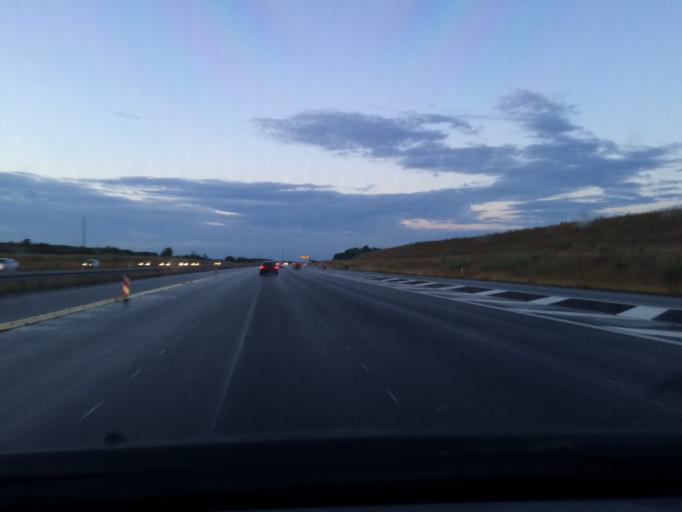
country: DK
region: Zealand
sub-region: Solrod Kommune
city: Solrod Strand
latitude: 55.5641
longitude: 12.2336
